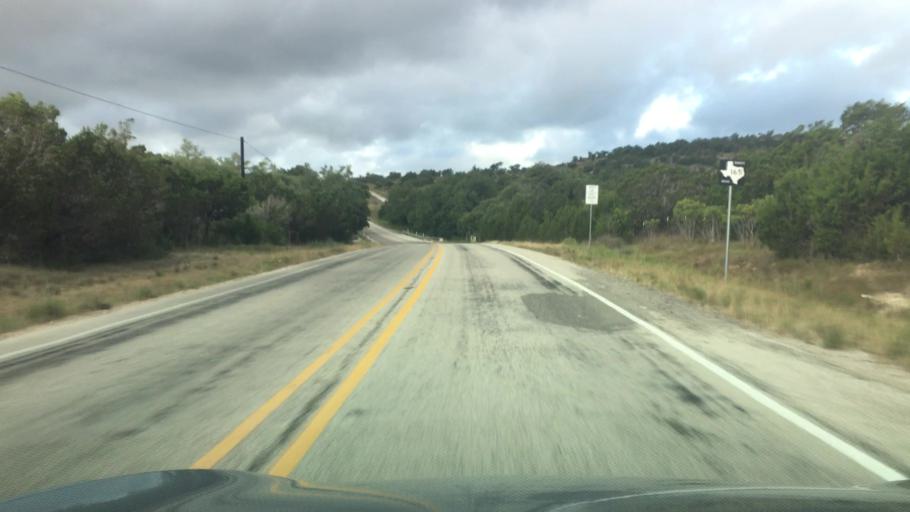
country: US
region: Texas
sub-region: Hays County
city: Dripping Springs
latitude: 30.1549
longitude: -98.2521
